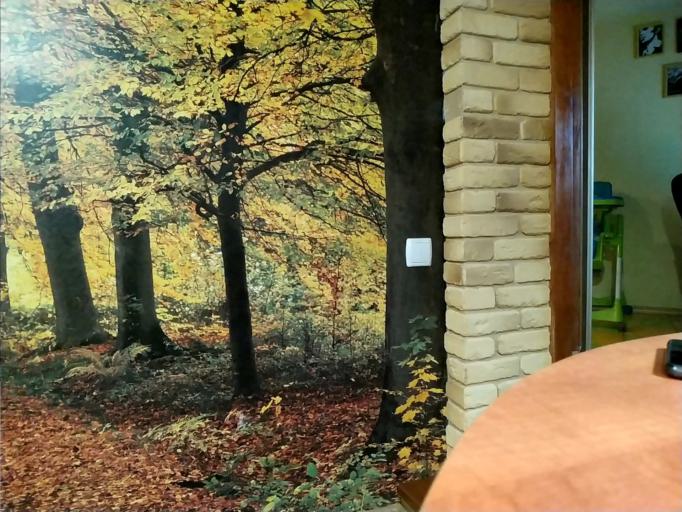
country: BY
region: Minsk
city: Il'ya
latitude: 54.4235
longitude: 27.5041
